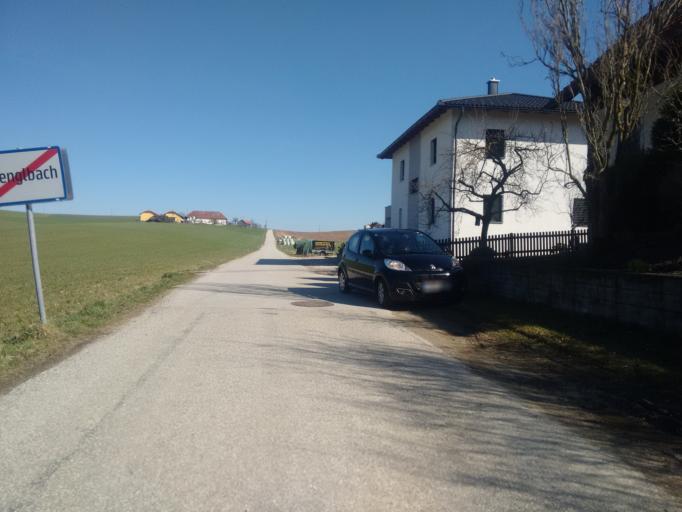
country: AT
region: Upper Austria
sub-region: Politischer Bezirk Grieskirchen
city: Bad Schallerbach
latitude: 48.2035
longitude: 13.9597
